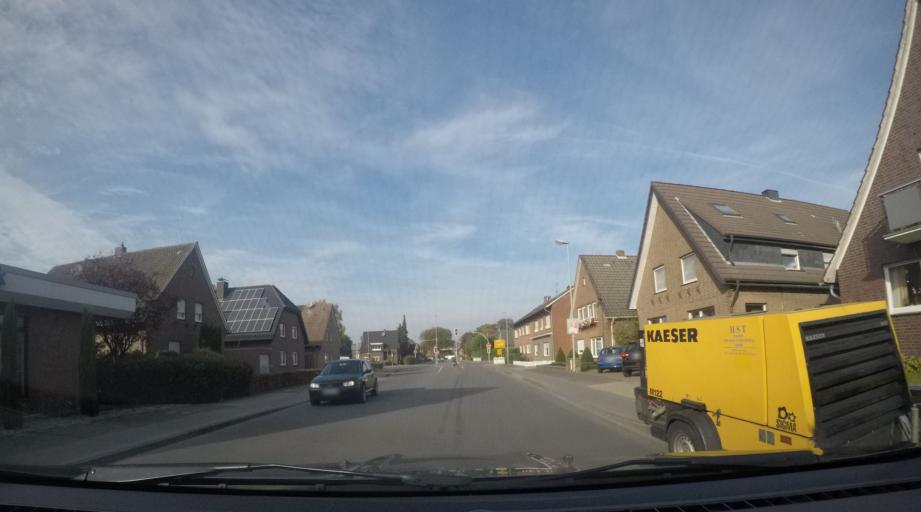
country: DE
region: North Rhine-Westphalia
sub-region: Regierungsbezirk Munster
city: Rhede
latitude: 51.8326
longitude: 6.6992
